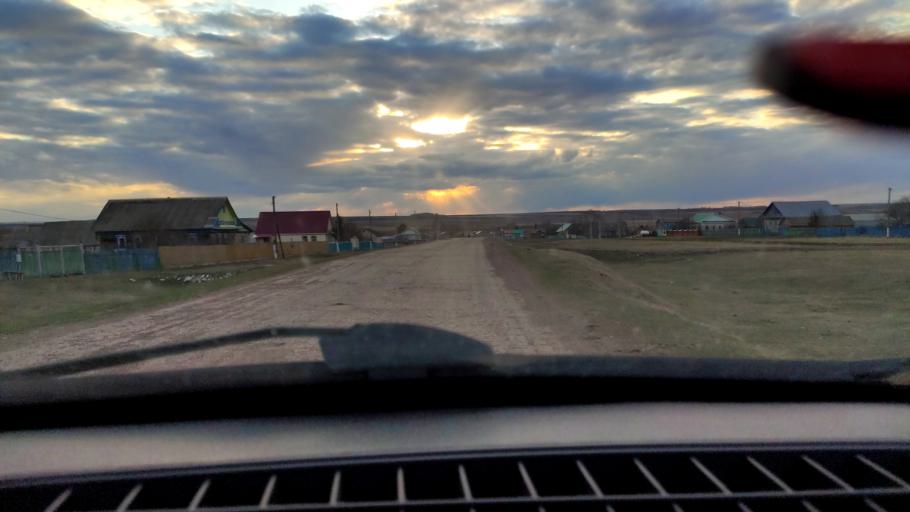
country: RU
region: Bashkortostan
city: Tolbazy
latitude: 54.0143
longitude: 55.5373
